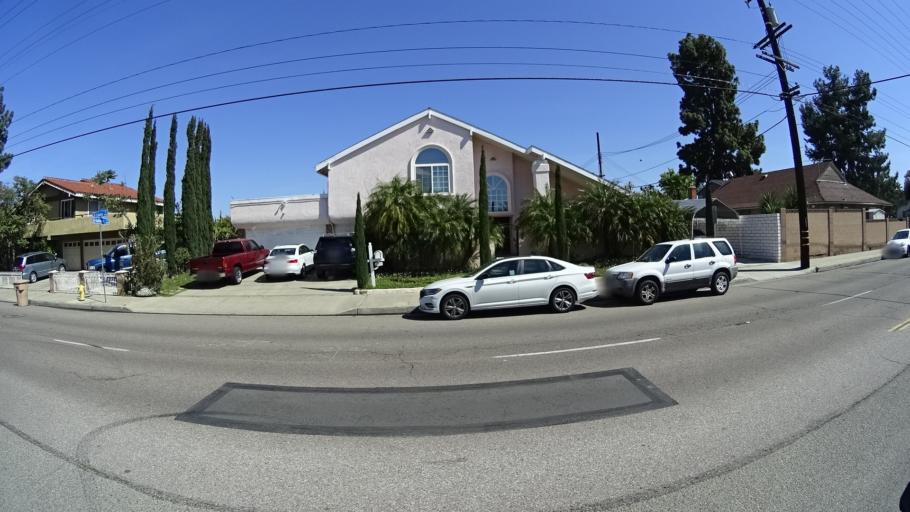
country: US
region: California
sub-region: Orange County
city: Villa Park
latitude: 33.8022
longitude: -117.8205
